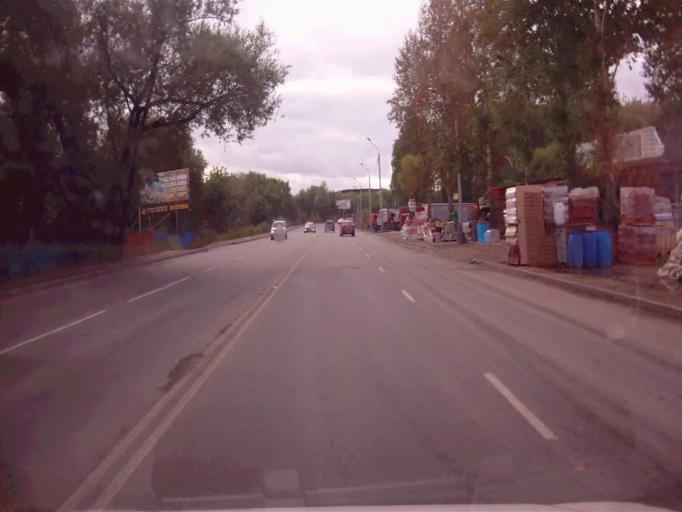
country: RU
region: Chelyabinsk
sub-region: Gorod Chelyabinsk
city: Chelyabinsk
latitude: 55.1473
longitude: 61.2983
